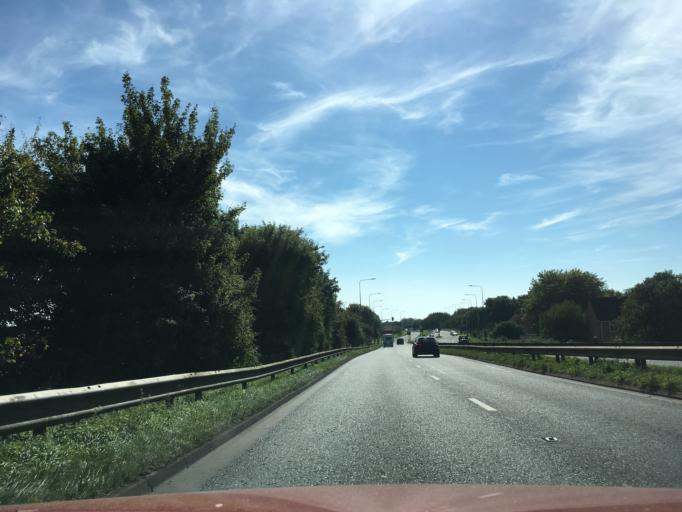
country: GB
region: England
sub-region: South Gloucestershire
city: Severn Beach
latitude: 51.5663
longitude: -2.6452
